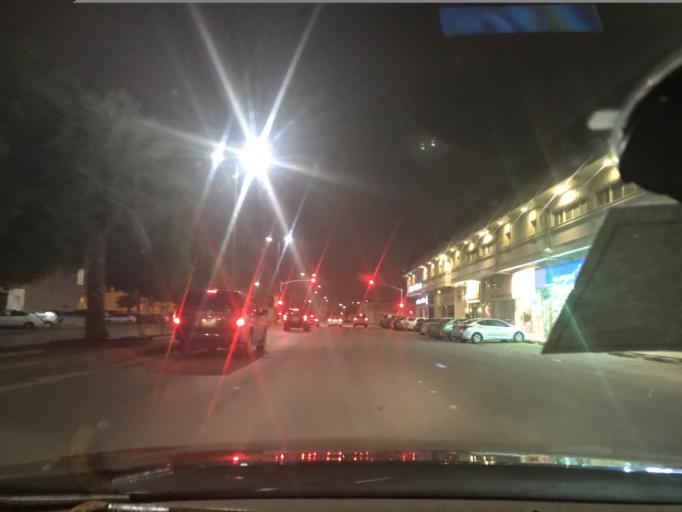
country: SA
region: Ar Riyad
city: Riyadh
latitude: 24.7079
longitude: 46.7743
